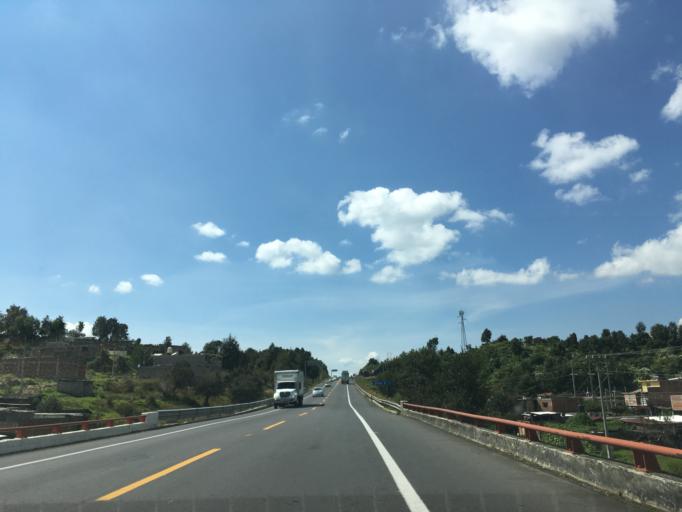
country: MX
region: Michoacan
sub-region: Patzcuaro
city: Colonia Vista Bella (Lomas del Peaje)
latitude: 19.4931
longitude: -101.6052
